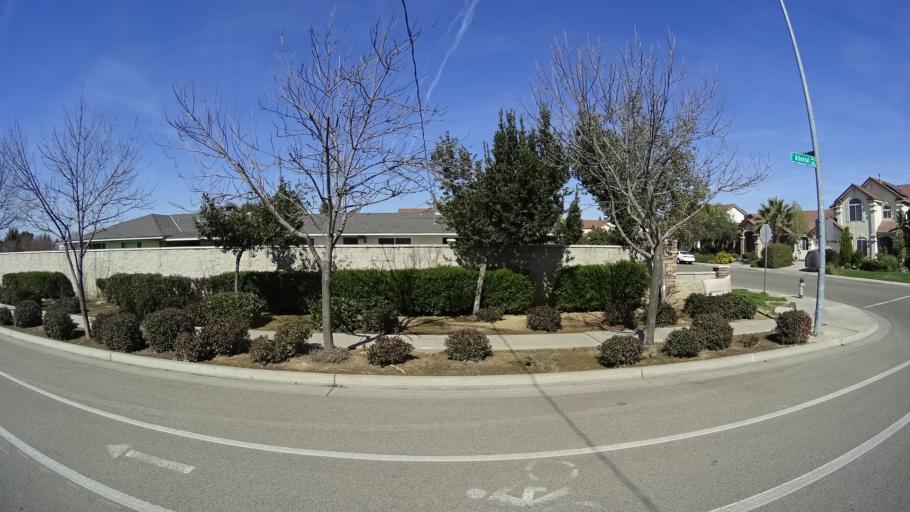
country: US
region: California
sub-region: Fresno County
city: Clovis
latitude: 36.8449
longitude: -119.7338
